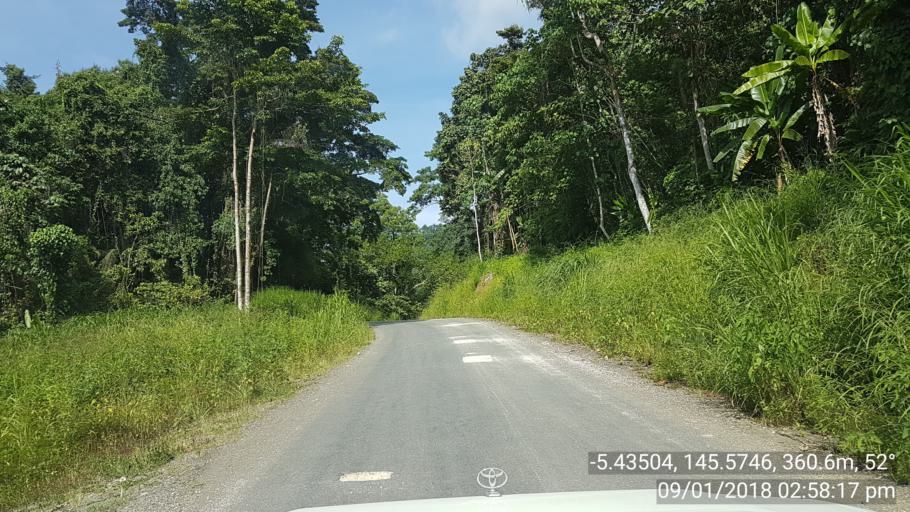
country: PG
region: Madang
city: Madang
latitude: -5.4353
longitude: 145.5744
